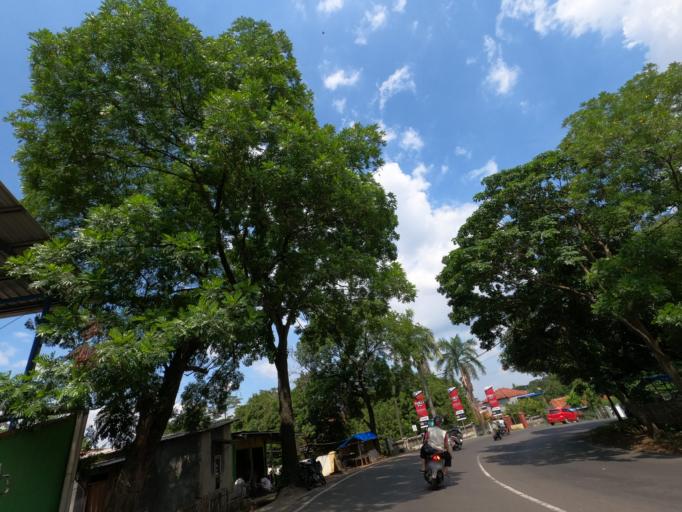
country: ID
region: West Java
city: Pamanukan
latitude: -6.5510
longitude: 107.7513
